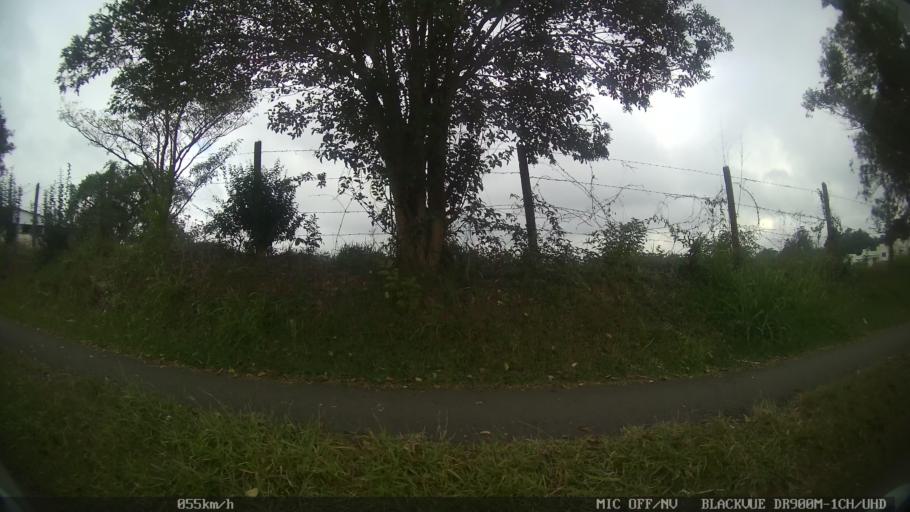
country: BR
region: Parana
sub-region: Almirante Tamandare
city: Almirante Tamandare
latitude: -25.3655
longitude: -49.2720
